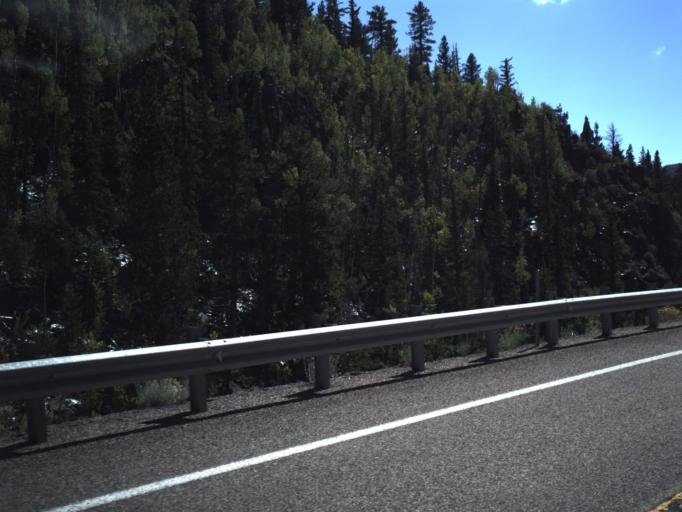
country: US
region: Utah
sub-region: Beaver County
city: Beaver
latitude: 38.2741
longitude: -112.4630
